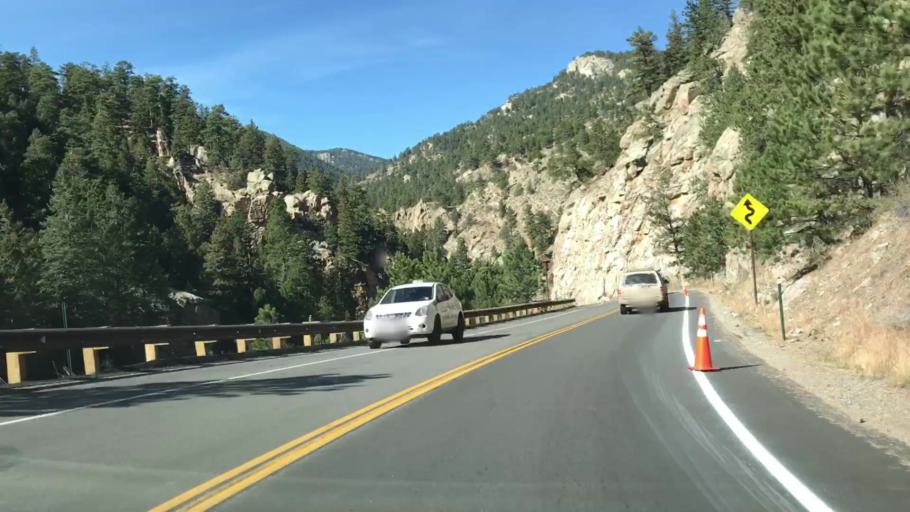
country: US
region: Colorado
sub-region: Larimer County
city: Estes Park
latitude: 40.4091
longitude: -105.3983
